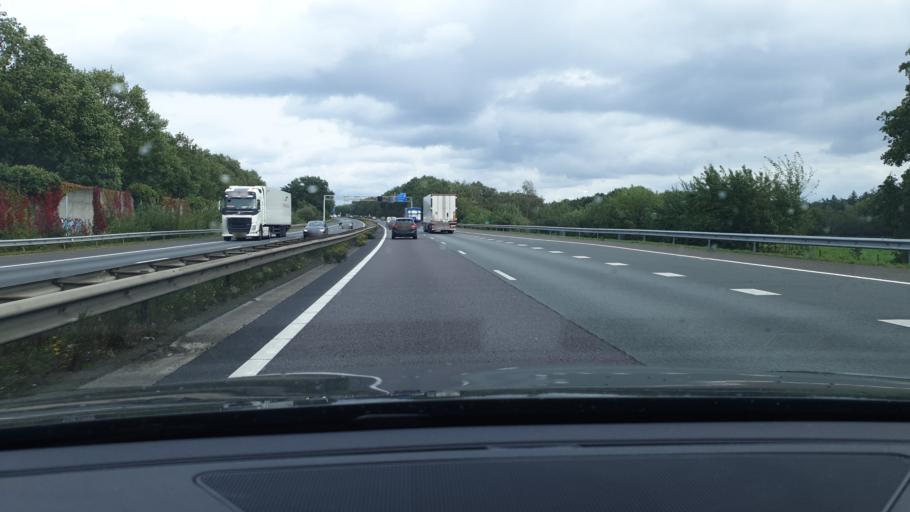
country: NL
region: North Brabant
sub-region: Gemeente Geldrop-Mierlo
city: Geldrop
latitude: 51.4043
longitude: 5.5499
